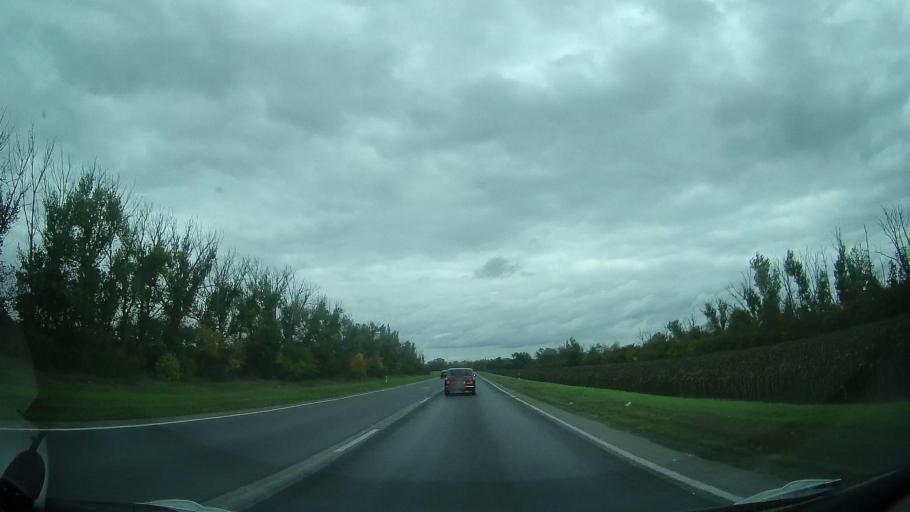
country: RU
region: Rostov
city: Yegorlykskaya
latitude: 46.5402
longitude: 40.7753
